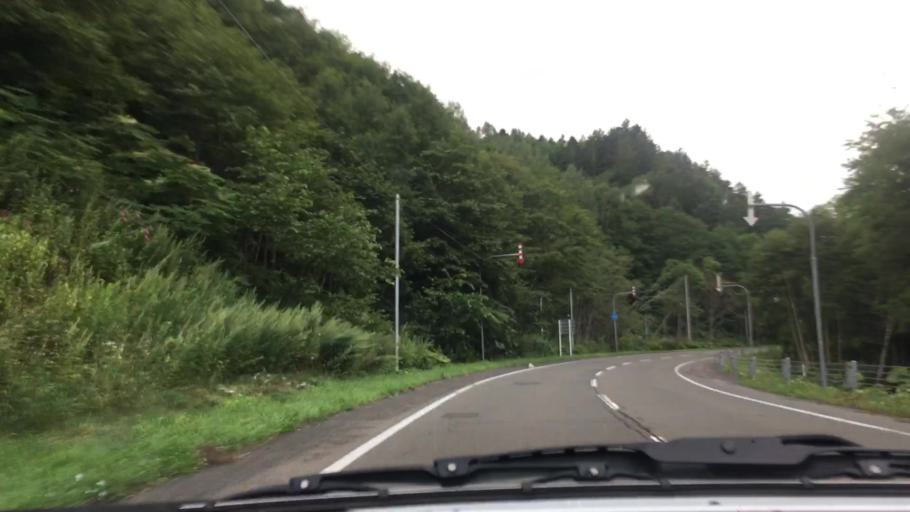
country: JP
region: Hokkaido
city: Shimo-furano
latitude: 43.0660
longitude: 142.6700
